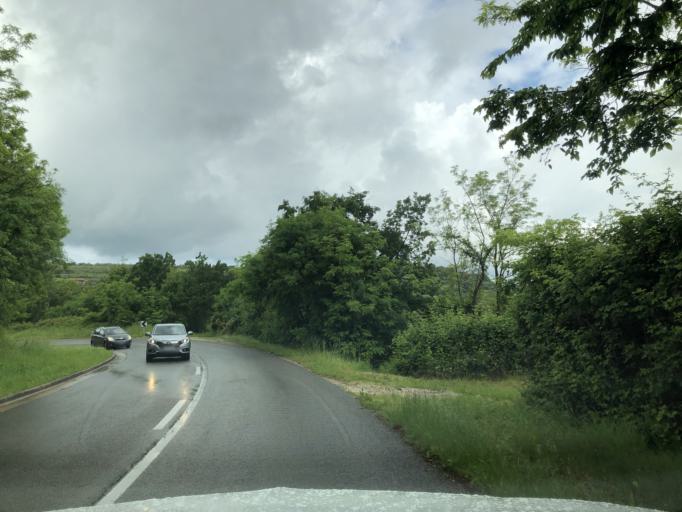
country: SI
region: Koper-Capodistria
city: Prade
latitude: 45.5038
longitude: 13.7758
